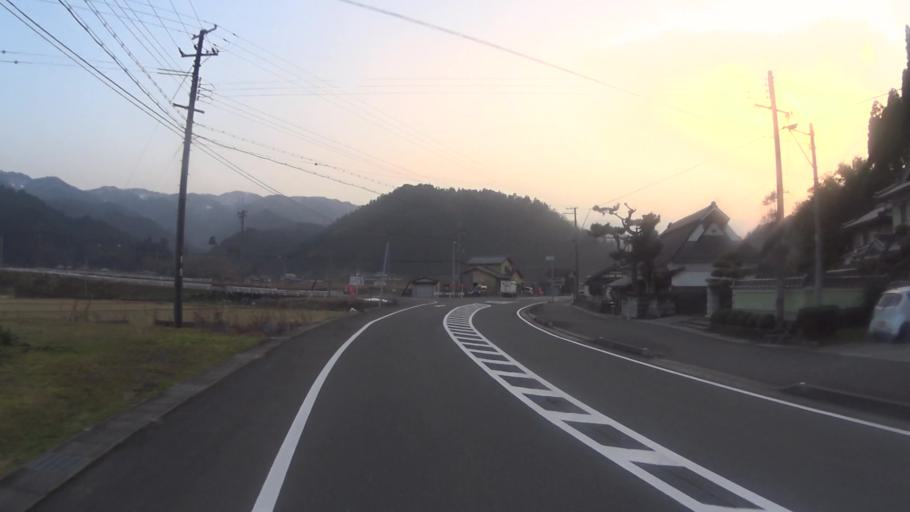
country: JP
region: Kyoto
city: Maizuru
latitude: 35.3734
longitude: 135.4424
